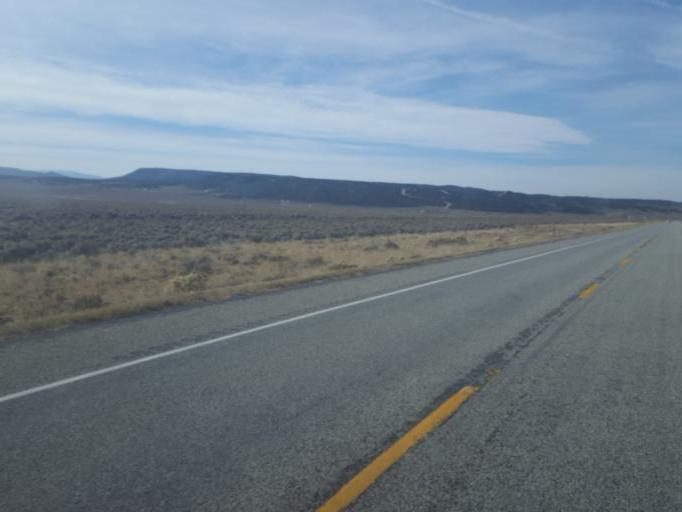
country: US
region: Colorado
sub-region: Costilla County
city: San Luis
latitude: 37.4431
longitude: -105.3802
